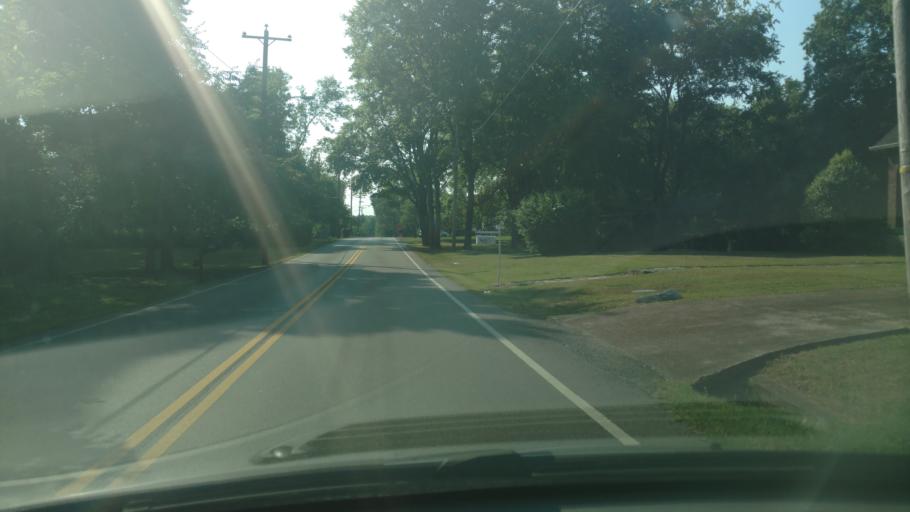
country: US
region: Tennessee
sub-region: Davidson County
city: Lakewood
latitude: 36.2216
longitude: -86.7176
